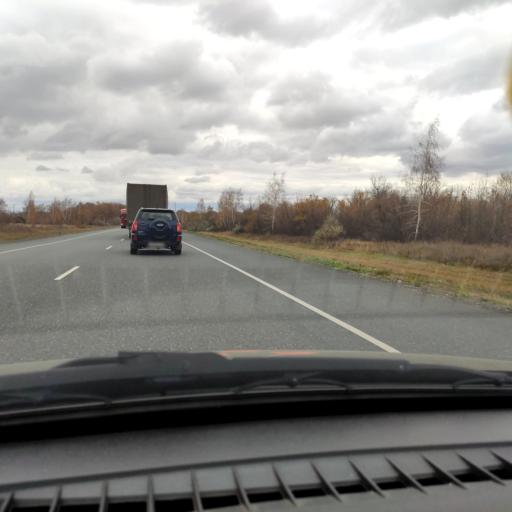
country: RU
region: Samara
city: Mezhdurechensk
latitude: 53.2415
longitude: 48.9727
